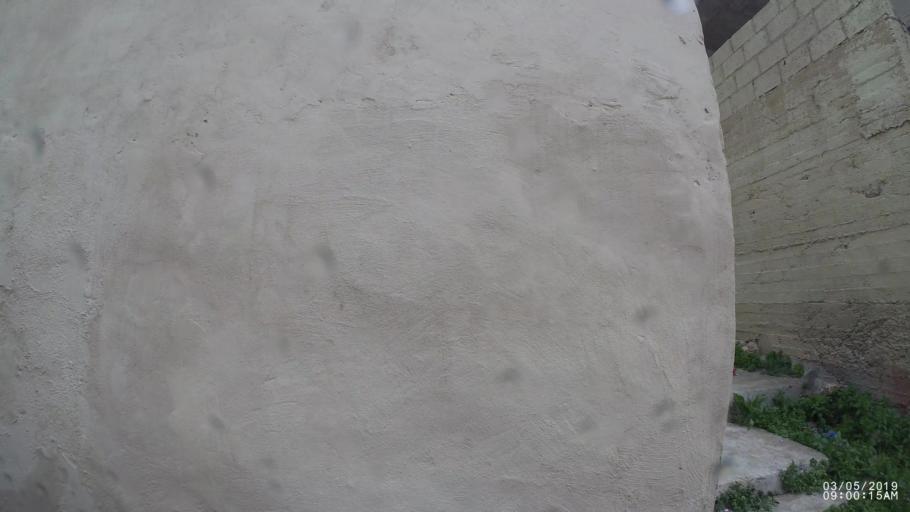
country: JO
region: Amman
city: Amman
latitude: 31.9572
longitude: 35.9401
